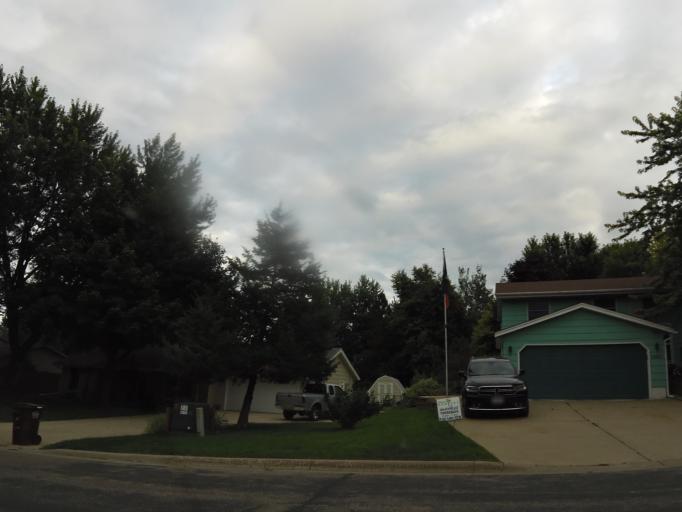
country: US
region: Minnesota
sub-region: Scott County
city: Prior Lake
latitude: 44.7063
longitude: -93.4225
